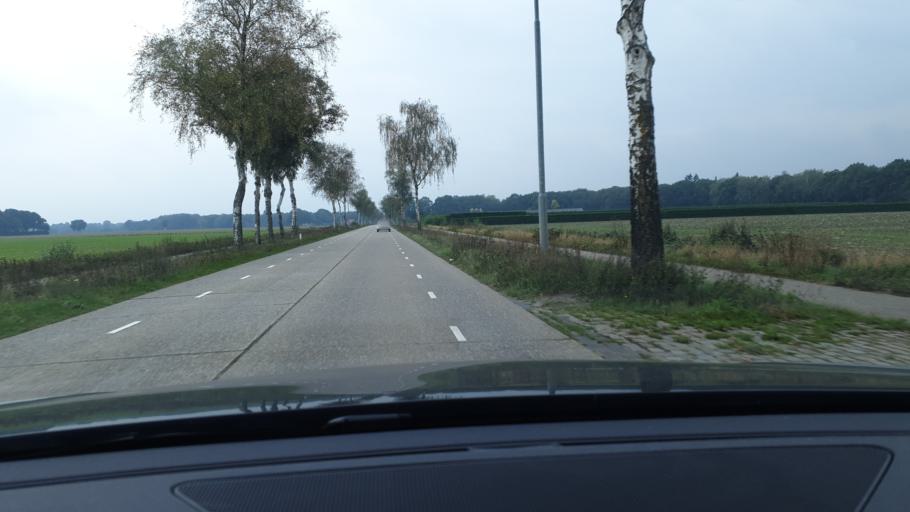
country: NL
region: North Brabant
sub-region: Gemeente Eersel
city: Eersel
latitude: 51.3744
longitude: 5.3452
